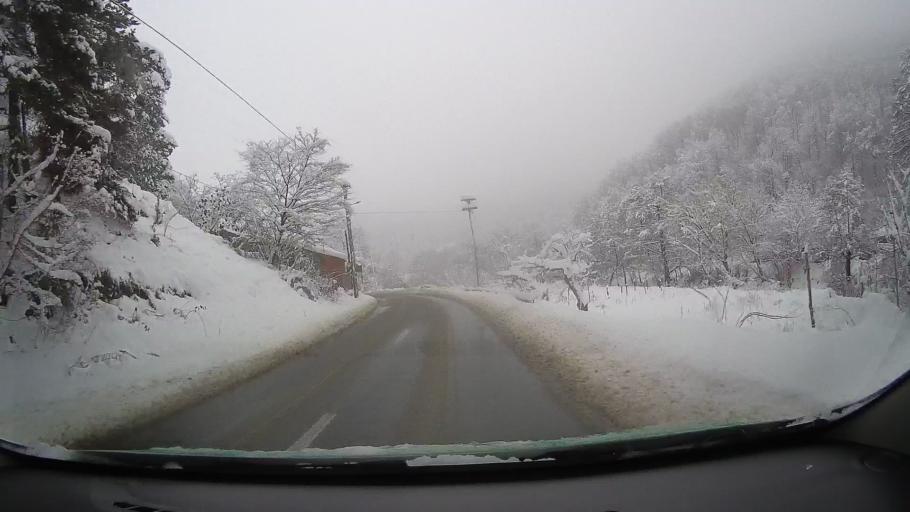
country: RO
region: Sibiu
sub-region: Comuna Tilisca
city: Tilisca
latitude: 45.7992
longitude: 23.8564
